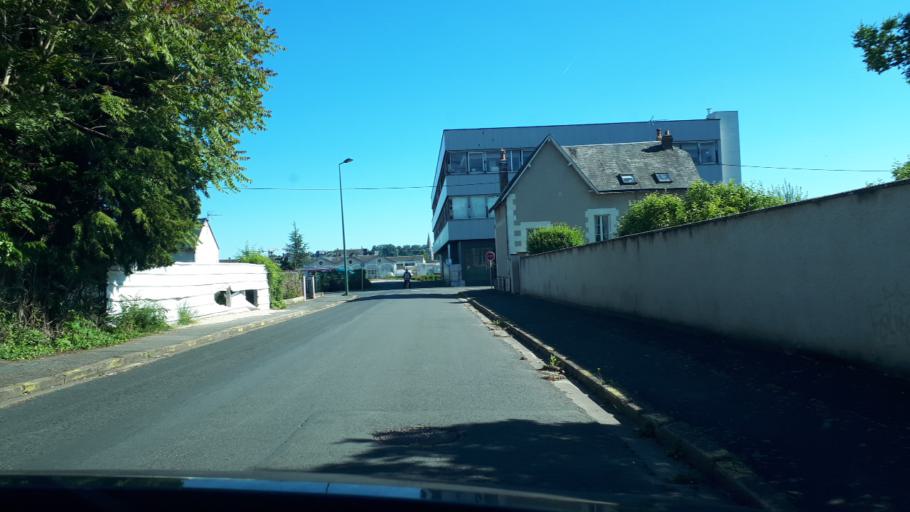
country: FR
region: Centre
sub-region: Departement du Loir-et-Cher
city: Vendome
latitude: 47.8039
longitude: 1.0663
